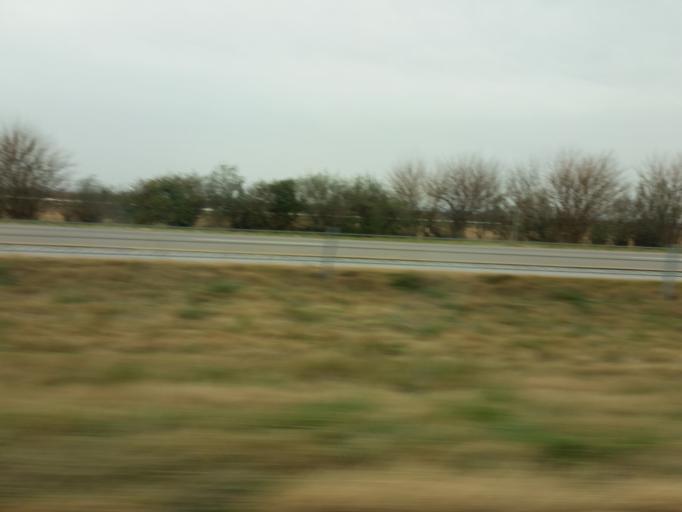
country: US
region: Iowa
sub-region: Scott County
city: Walcott
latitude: 41.6256
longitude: -90.8154
